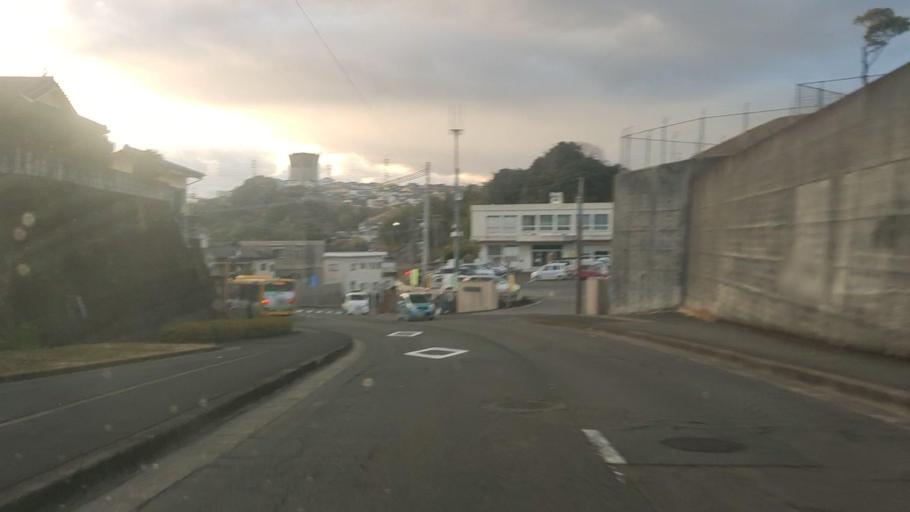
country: JP
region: Kagoshima
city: Kagoshima-shi
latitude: 31.6270
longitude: 130.5479
